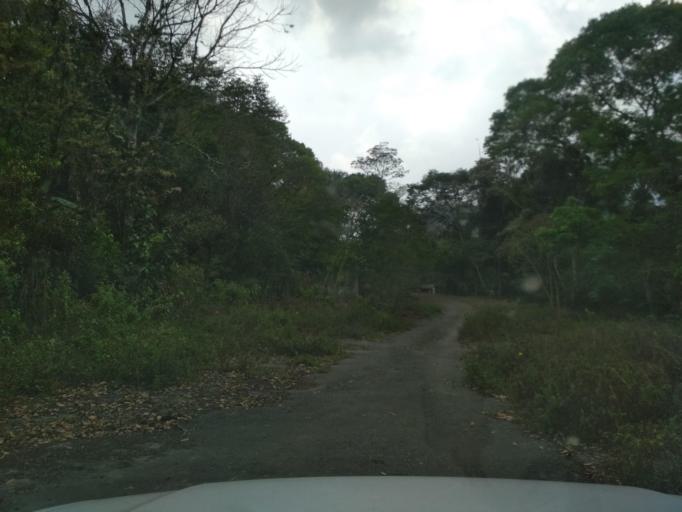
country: MX
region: Veracruz
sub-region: Cordoba
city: San Jose de Tapia
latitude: 18.8357
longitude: -96.9811
